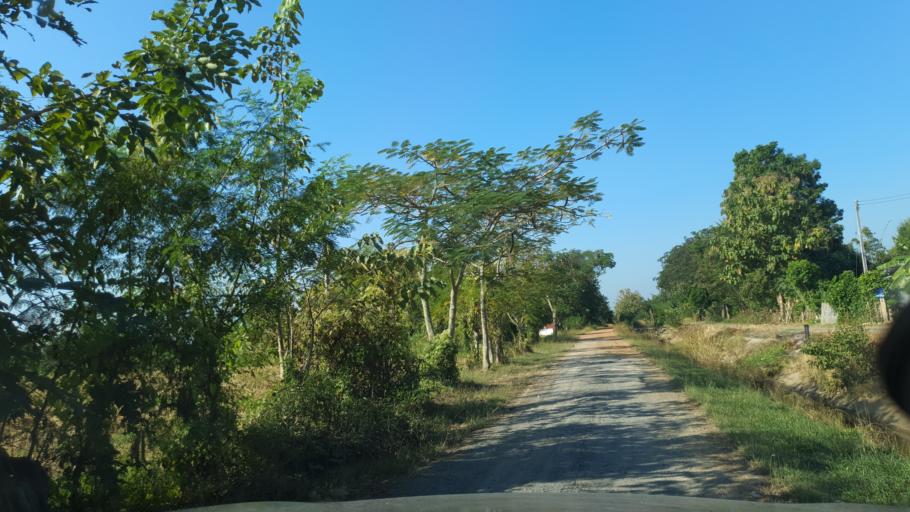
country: TH
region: Chiang Mai
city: San Kamphaeng
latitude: 18.7350
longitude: 99.1573
